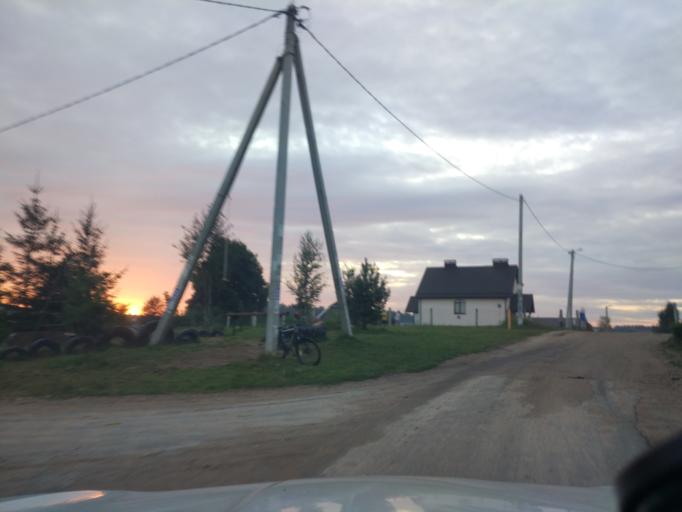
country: BY
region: Minsk
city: Astrashytski Haradok
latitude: 54.0845
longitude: 27.7016
